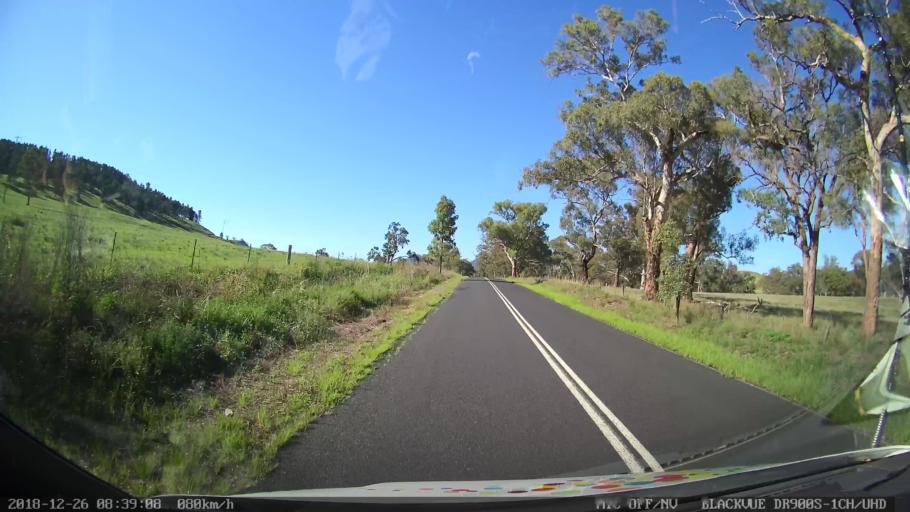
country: AU
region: New South Wales
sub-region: Upper Hunter Shire
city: Merriwa
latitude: -32.4499
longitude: 150.0764
